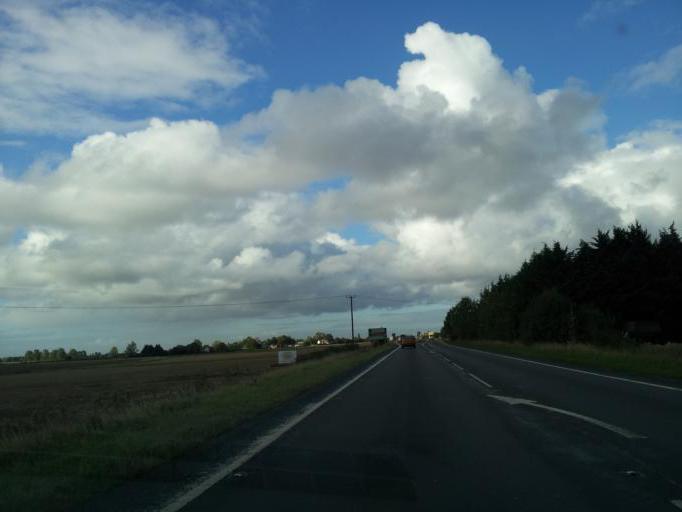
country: GB
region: England
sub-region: Norfolk
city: Terrington St Clement
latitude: 52.7466
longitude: 0.2738
